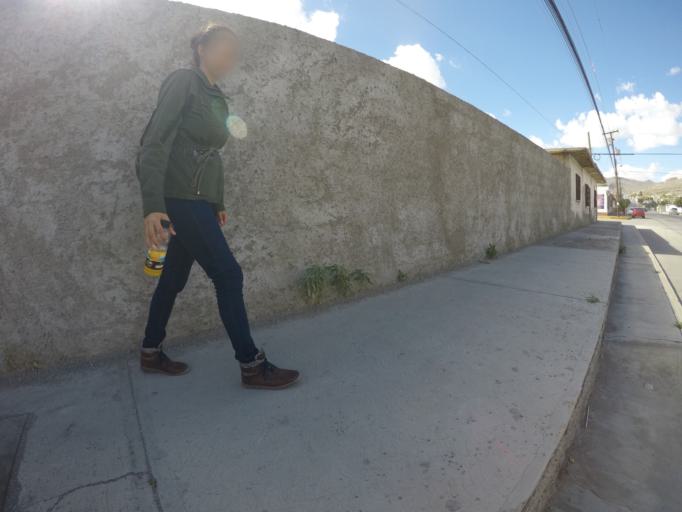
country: MX
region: Chihuahua
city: Ciudad Juarez
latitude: 31.6898
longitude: -106.4824
